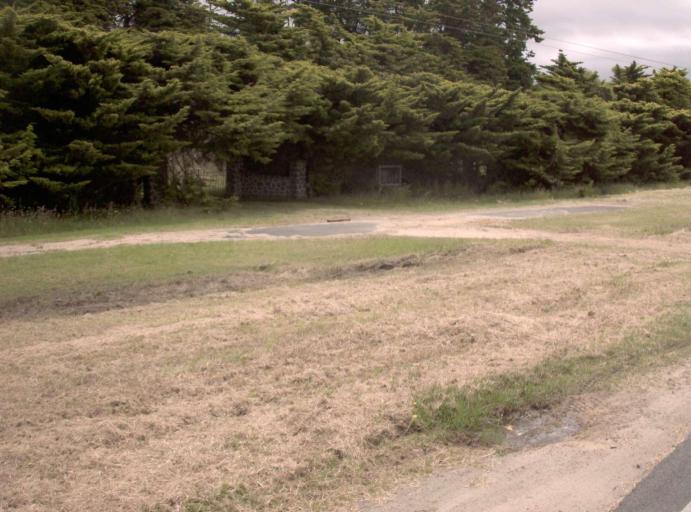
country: AU
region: Victoria
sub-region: Latrobe
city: Traralgon
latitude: -38.5526
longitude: 146.6543
